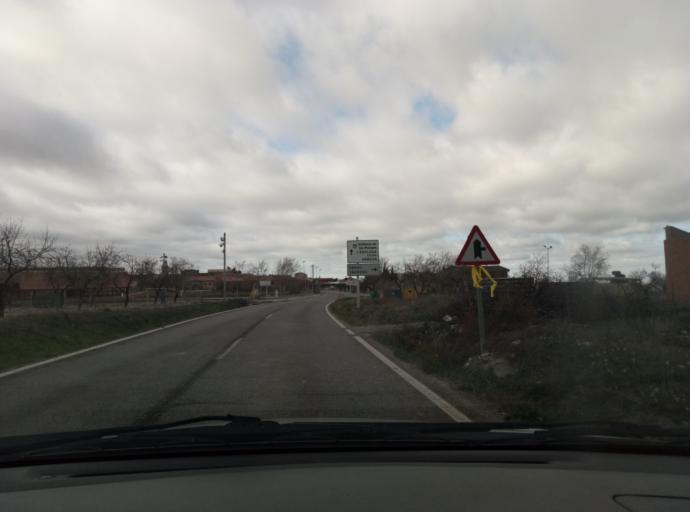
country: ES
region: Catalonia
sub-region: Provincia de Lleida
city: Vallbona de les Monges
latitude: 41.5615
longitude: 1.0626
